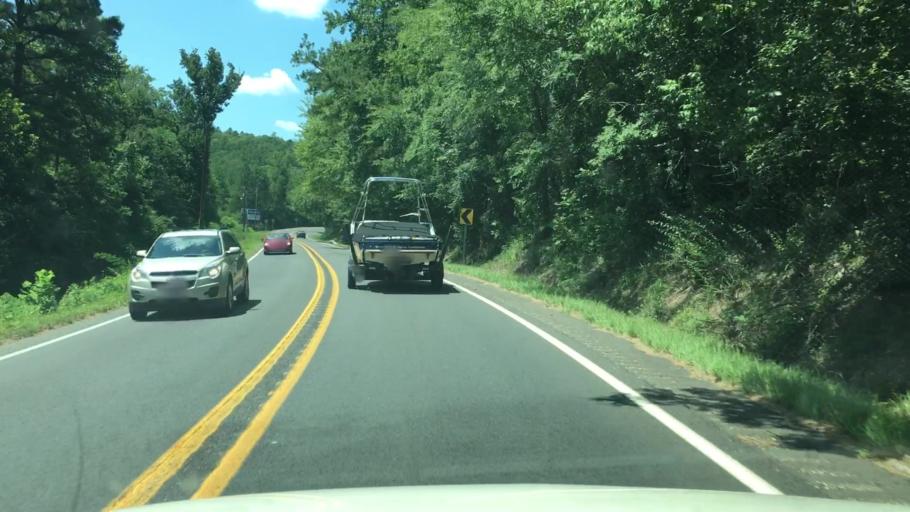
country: US
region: Arkansas
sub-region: Garland County
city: Lake Hamilton
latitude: 34.3385
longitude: -93.1809
